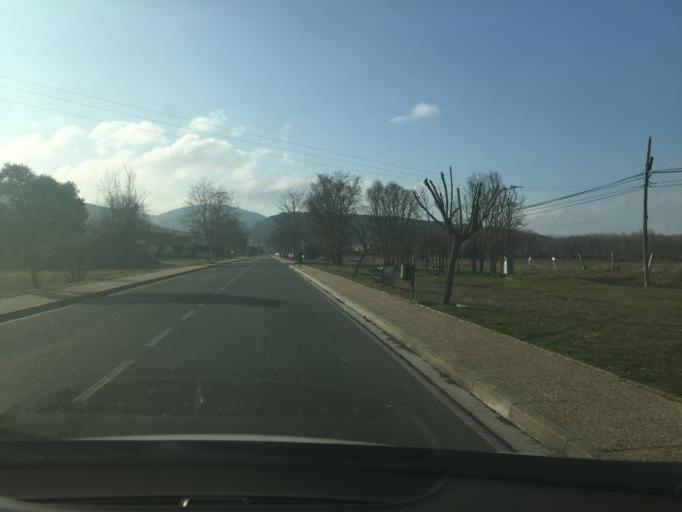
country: ES
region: Castille and Leon
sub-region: Provincia de Burgos
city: Medina de Pomar
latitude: 42.9382
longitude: -3.5800
